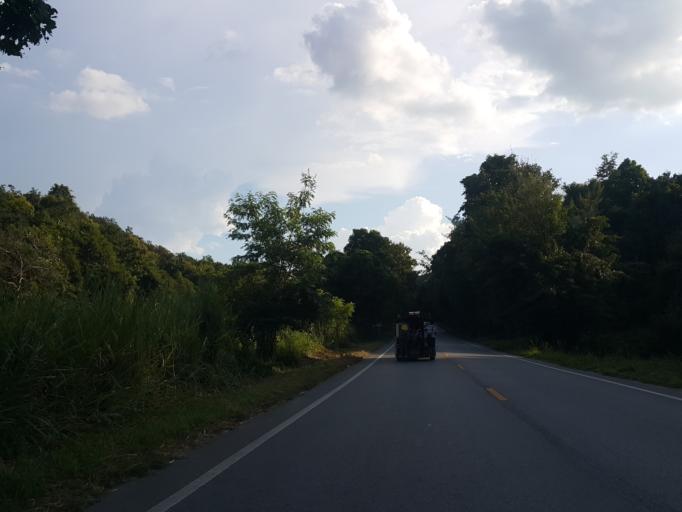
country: TH
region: Chiang Mai
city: Mae Taeng
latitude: 19.0857
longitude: 98.9818
